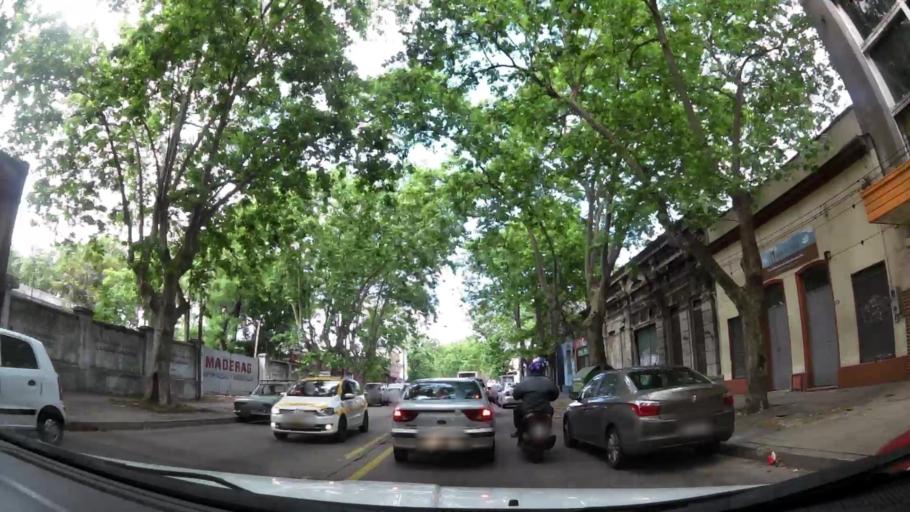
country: UY
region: Montevideo
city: Montevideo
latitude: -34.8749
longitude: -56.1846
